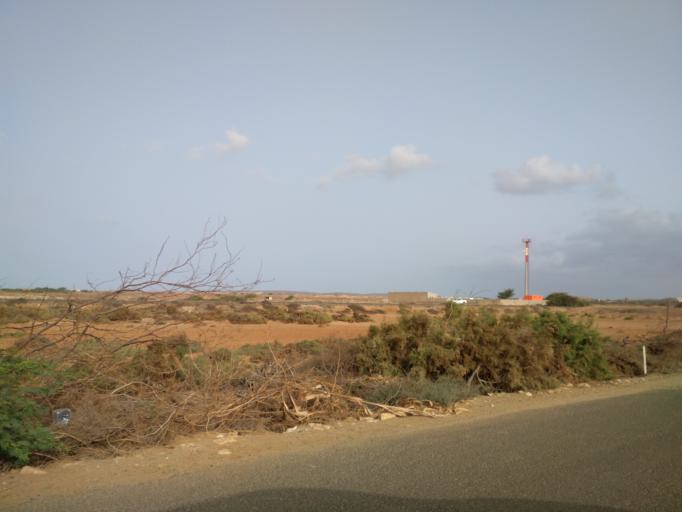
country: CV
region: Sal
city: Espargos
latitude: 16.6754
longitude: -22.9344
